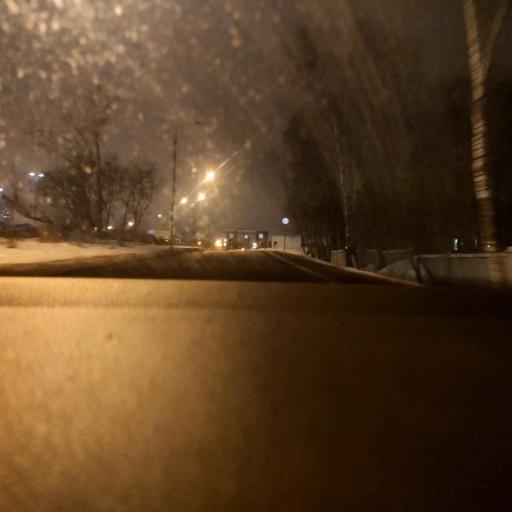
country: RU
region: Moskovskaya
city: Vostryakovo
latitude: 55.6603
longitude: 37.4521
